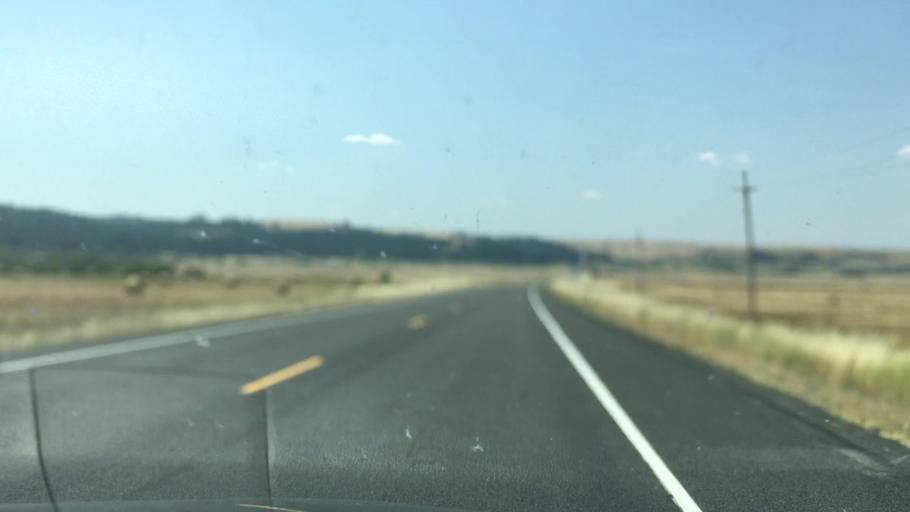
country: US
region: Idaho
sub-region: Idaho County
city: Grangeville
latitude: 45.8922
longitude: -116.1933
